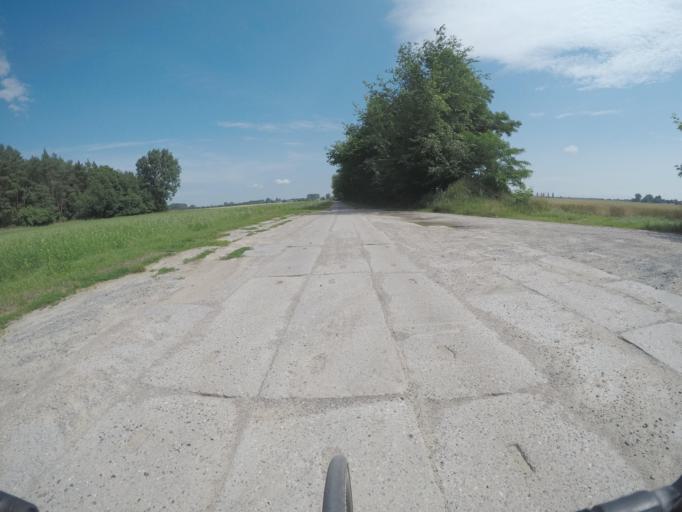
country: DE
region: Mecklenburg-Vorpommern
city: Rambin
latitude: 54.3617
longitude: 13.1773
